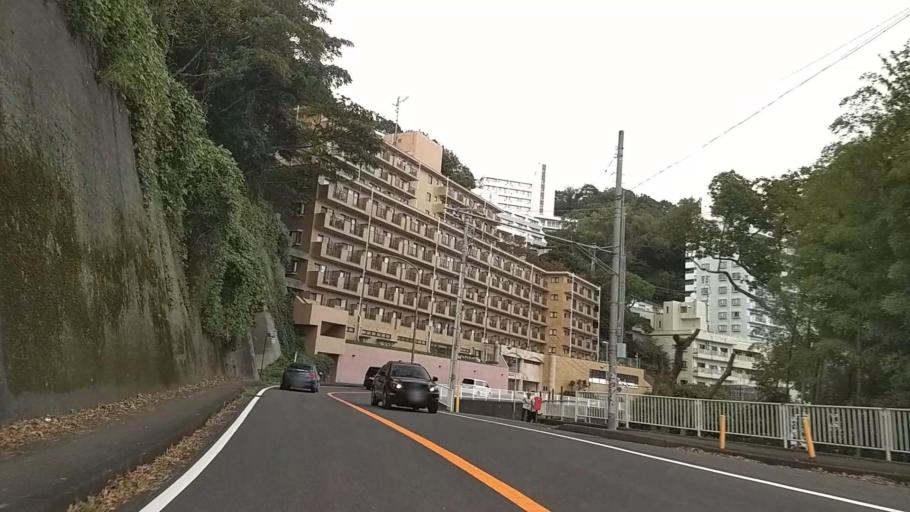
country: JP
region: Shizuoka
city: Atami
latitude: 35.1059
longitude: 139.0839
